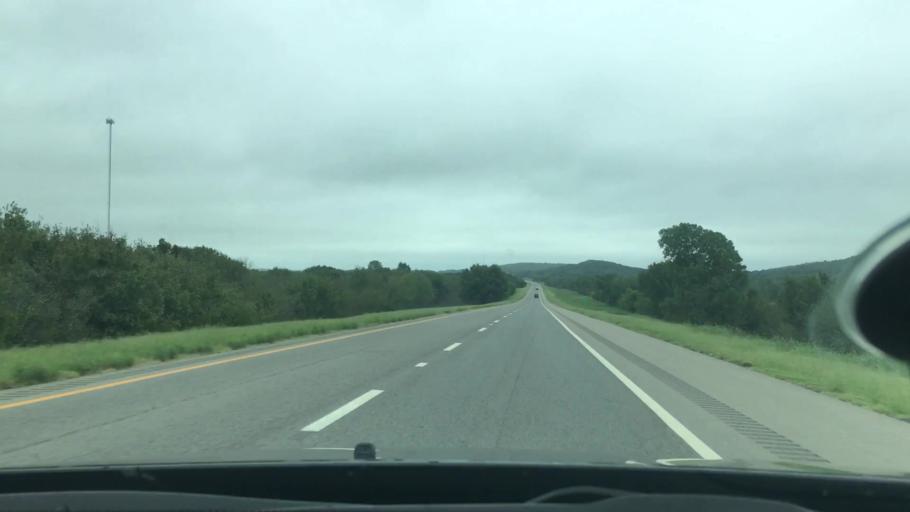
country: US
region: Oklahoma
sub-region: McIntosh County
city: Checotah
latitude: 35.4570
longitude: -95.4204
